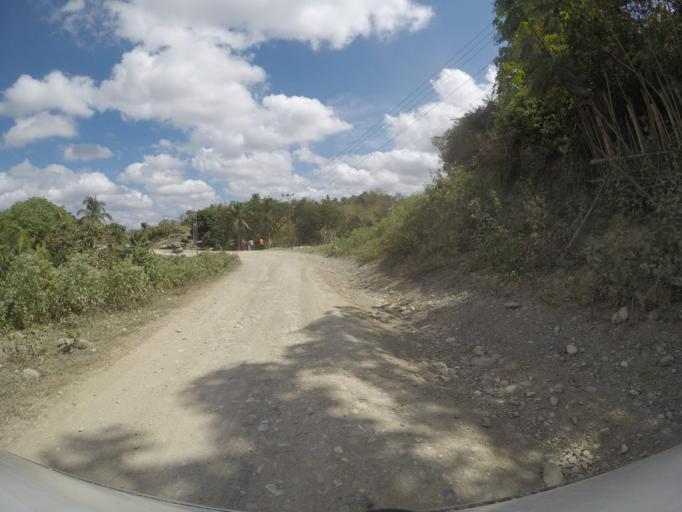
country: TL
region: Viqueque
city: Viqueque
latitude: -8.8702
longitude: 126.3435
